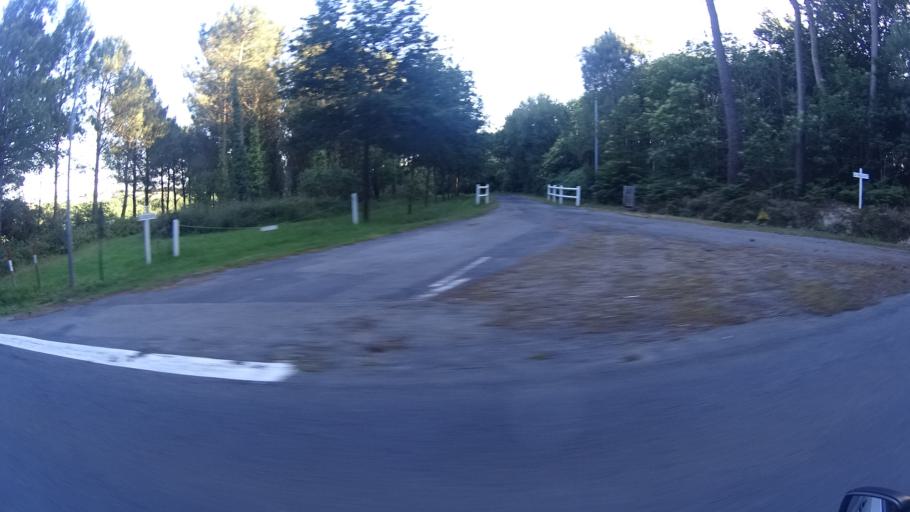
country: FR
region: Brittany
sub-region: Departement d'Ille-et-Vilaine
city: Grand-Fougeray
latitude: 47.7389
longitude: -1.7885
